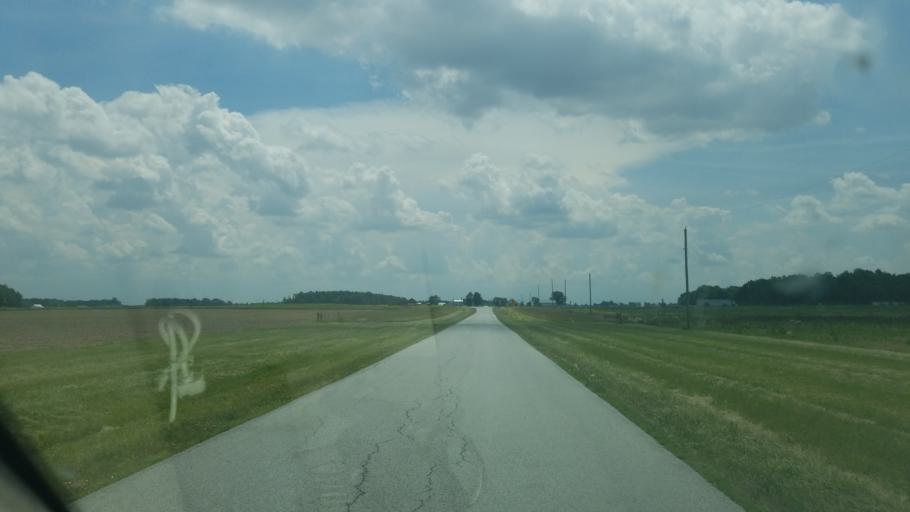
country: US
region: Ohio
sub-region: Hancock County
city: Arlington
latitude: 40.8309
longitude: -83.6000
